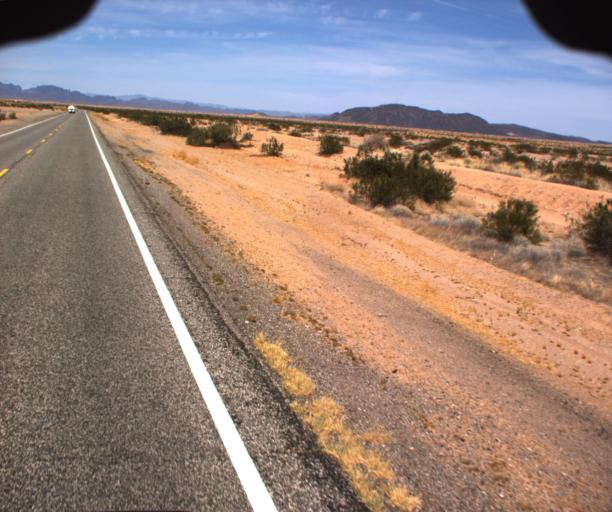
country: US
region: Arizona
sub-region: La Paz County
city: Parker
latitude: 34.0581
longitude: -114.2576
